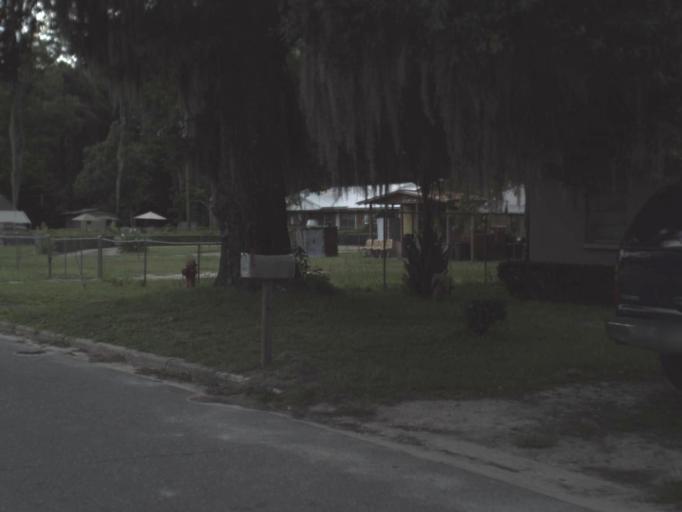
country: US
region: Florida
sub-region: Bradford County
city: Starke
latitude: 30.0432
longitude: -82.0677
